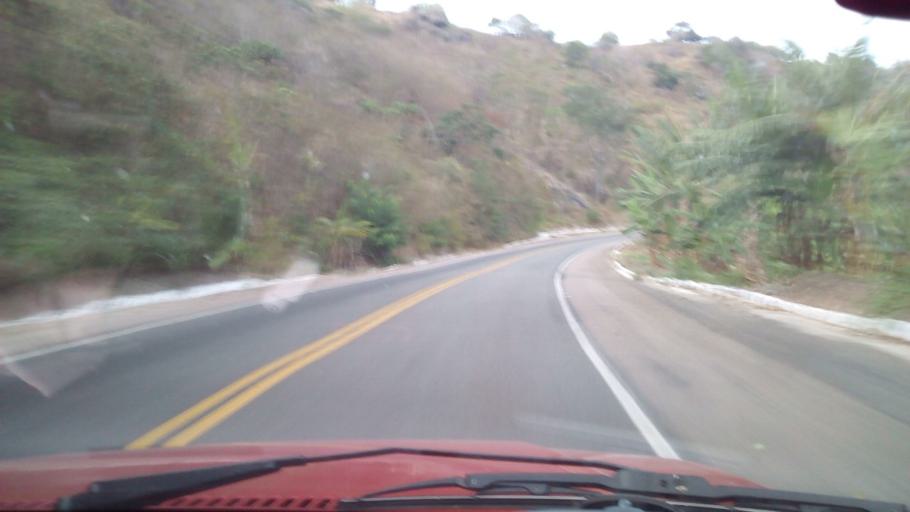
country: BR
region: Paraiba
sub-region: Bananeiras
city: Solanea
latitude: -6.7429
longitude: -35.5647
